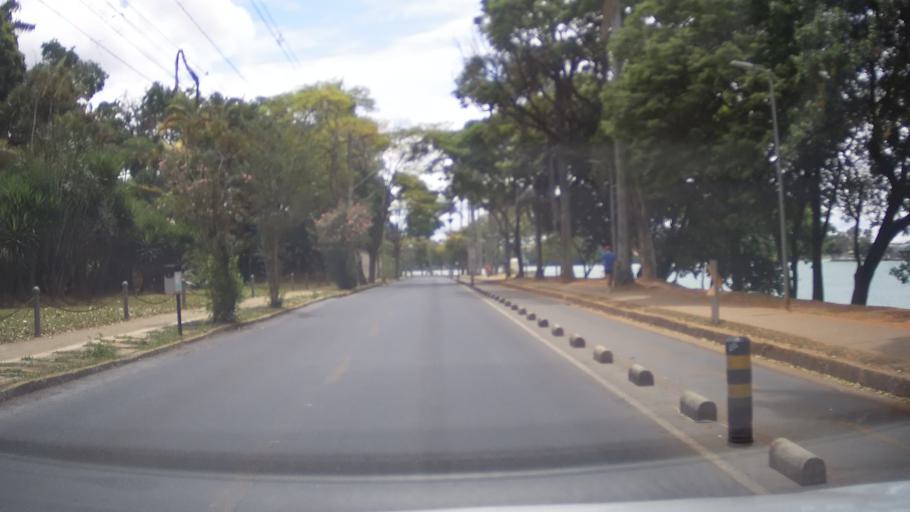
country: BR
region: Minas Gerais
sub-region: Belo Horizonte
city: Belo Horizonte
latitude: -19.8567
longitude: -43.9808
